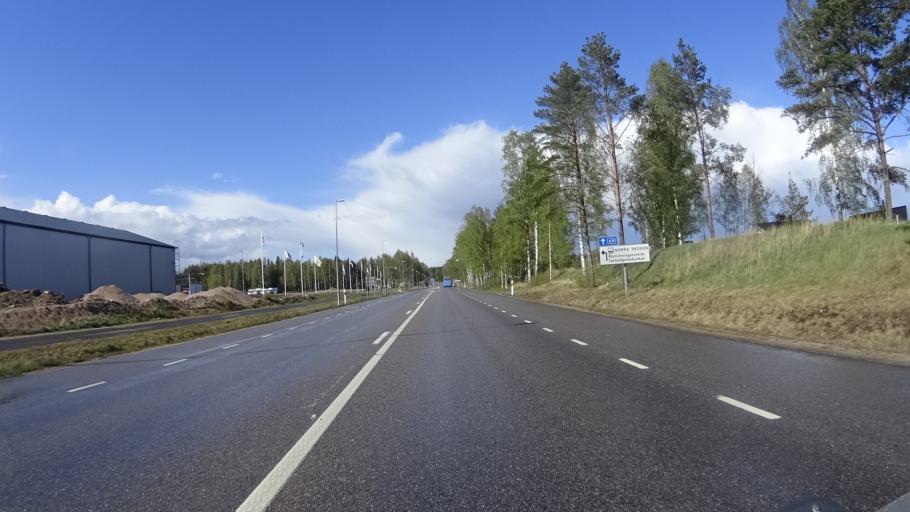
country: SE
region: Vaestra Goetaland
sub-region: Karlsborgs Kommun
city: Karlsborg
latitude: 58.5505
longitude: 14.4996
